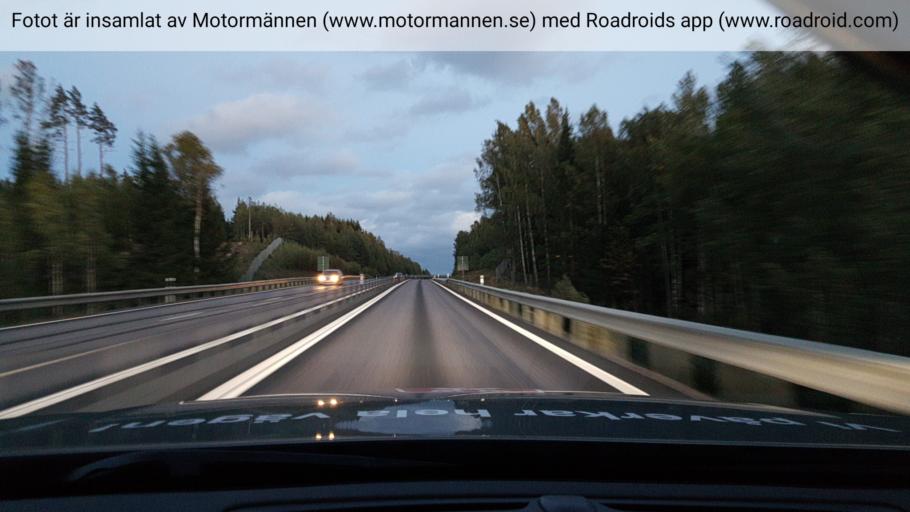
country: SE
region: Vaermland
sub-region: Karlstads Kommun
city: Skattkarr
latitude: 59.4000
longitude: 13.7933
